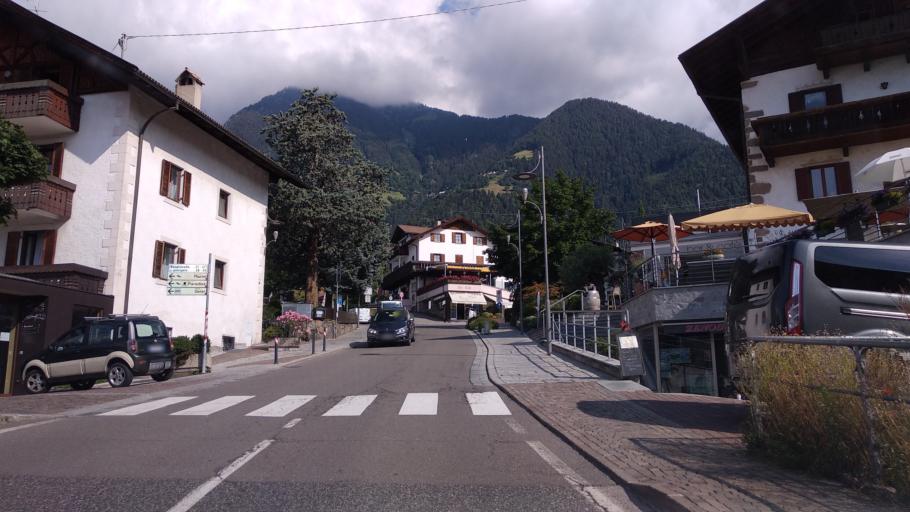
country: IT
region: Trentino-Alto Adige
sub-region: Bolzano
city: Tirolo
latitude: 46.6893
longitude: 11.1557
